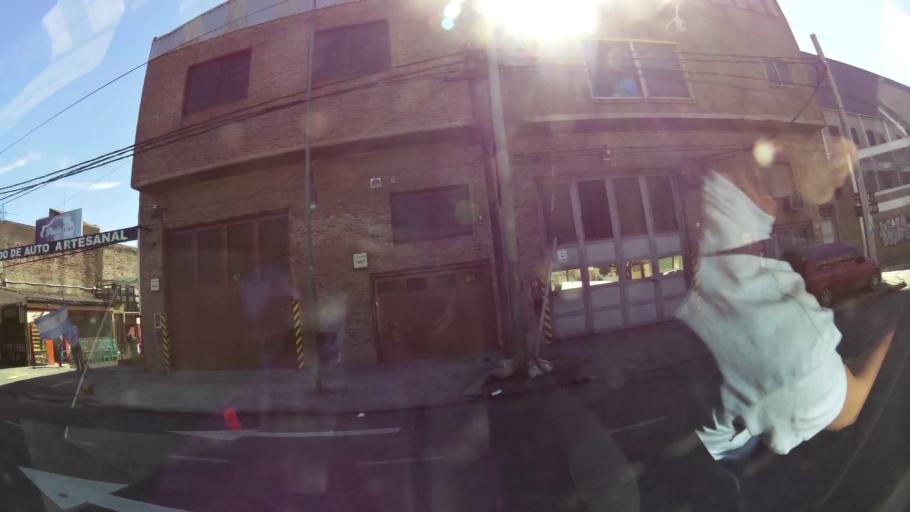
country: AR
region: Buenos Aires
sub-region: Partido de General San Martin
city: General San Martin
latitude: -34.5437
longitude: -58.5278
